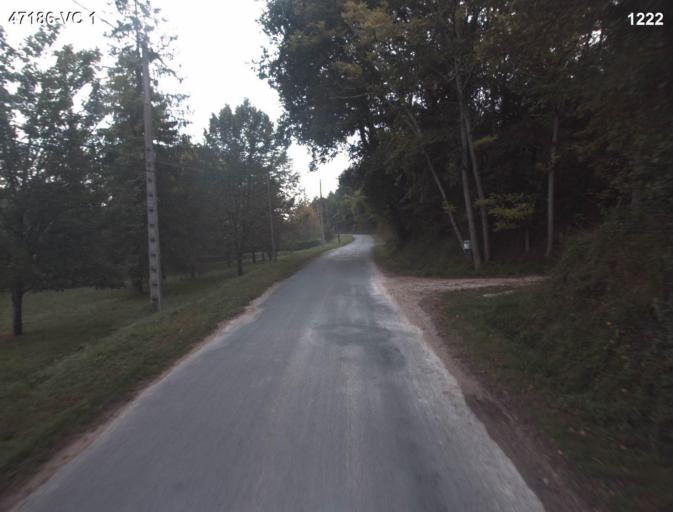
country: FR
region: Aquitaine
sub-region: Departement du Lot-et-Garonne
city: Port-Sainte-Marie
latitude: 44.1980
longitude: 0.4378
